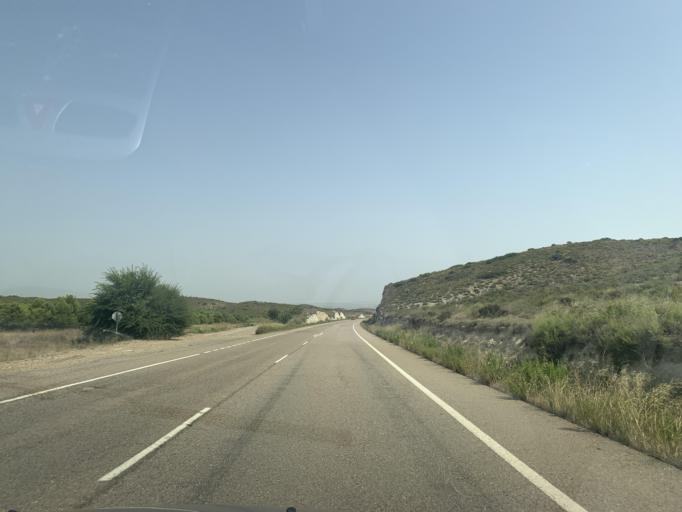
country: ES
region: Aragon
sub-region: Provincia de Zaragoza
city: El Burgo de Ebro
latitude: 41.5004
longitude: -0.7133
